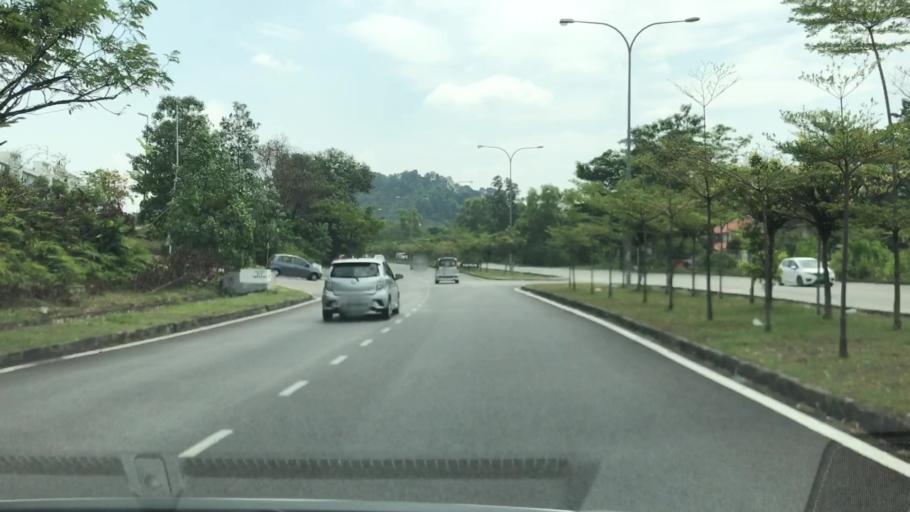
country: MY
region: Putrajaya
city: Putrajaya
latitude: 3.0077
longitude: 101.6704
